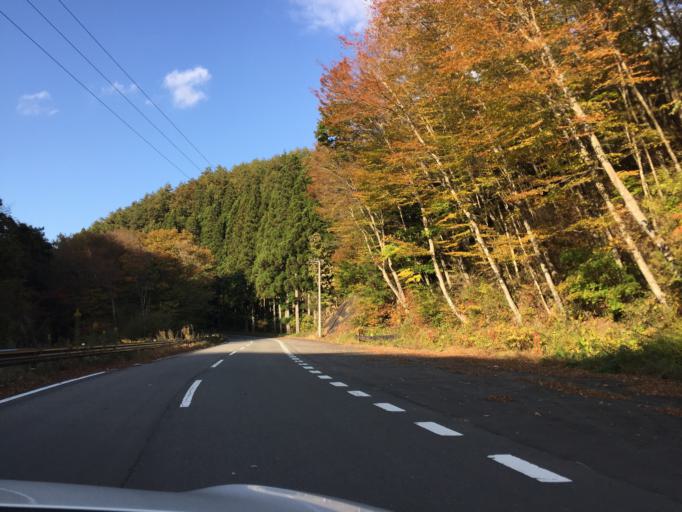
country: JP
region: Fukushima
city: Iwaki
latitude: 37.2515
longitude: 140.7604
